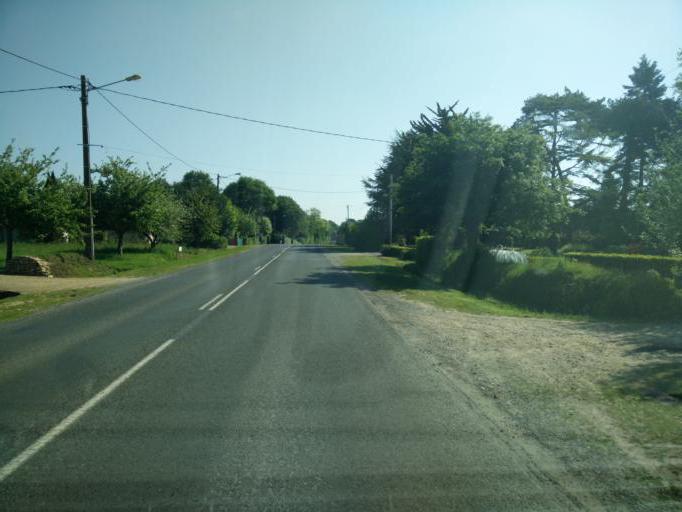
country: FR
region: Brittany
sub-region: Departement du Morbihan
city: Branderion
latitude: 47.8267
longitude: -3.1965
